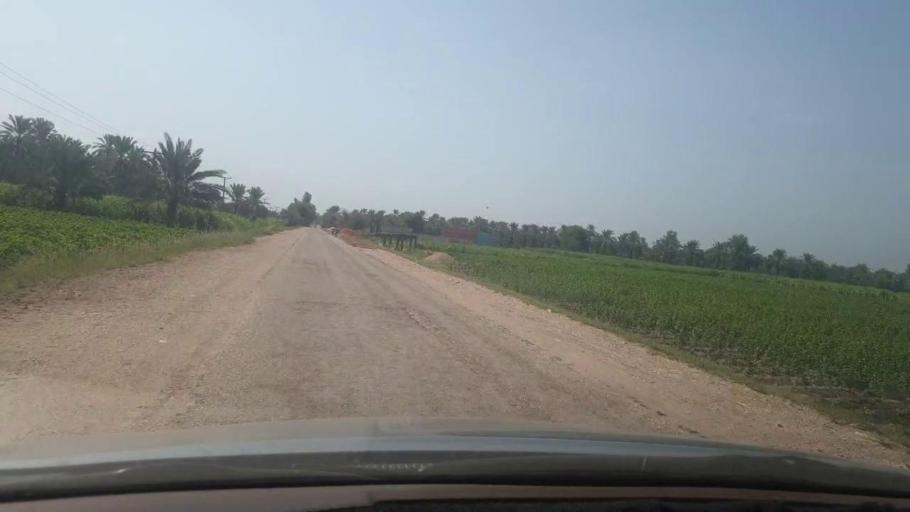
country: PK
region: Sindh
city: Ranipur
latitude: 27.2888
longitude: 68.5770
